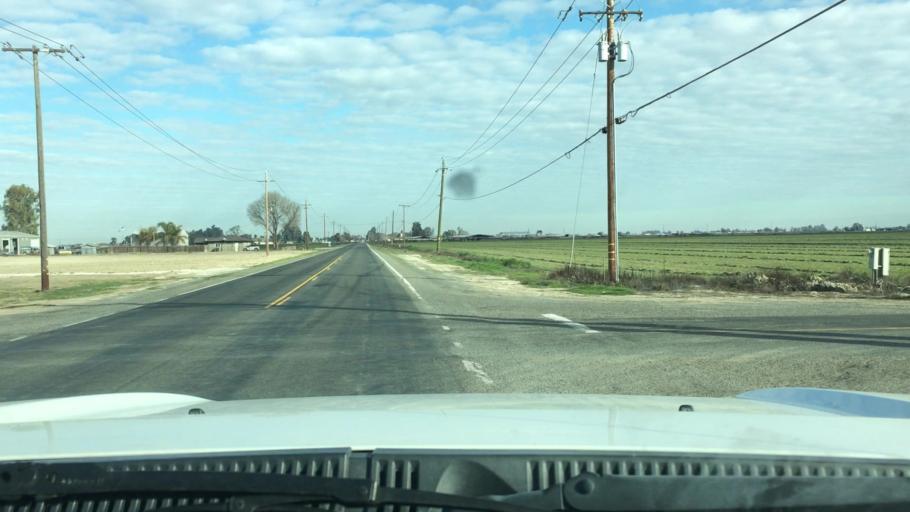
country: US
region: California
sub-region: Kings County
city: Stratford
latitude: 36.2258
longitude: -119.7803
